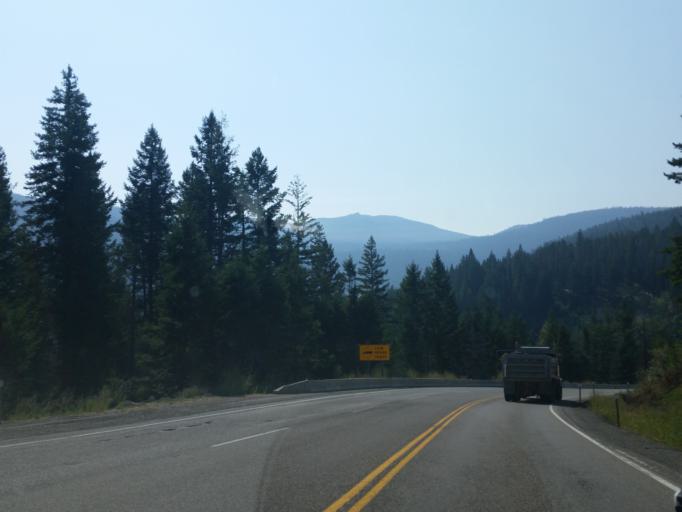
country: CA
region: British Columbia
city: Princeton
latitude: 49.1920
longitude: -120.5596
